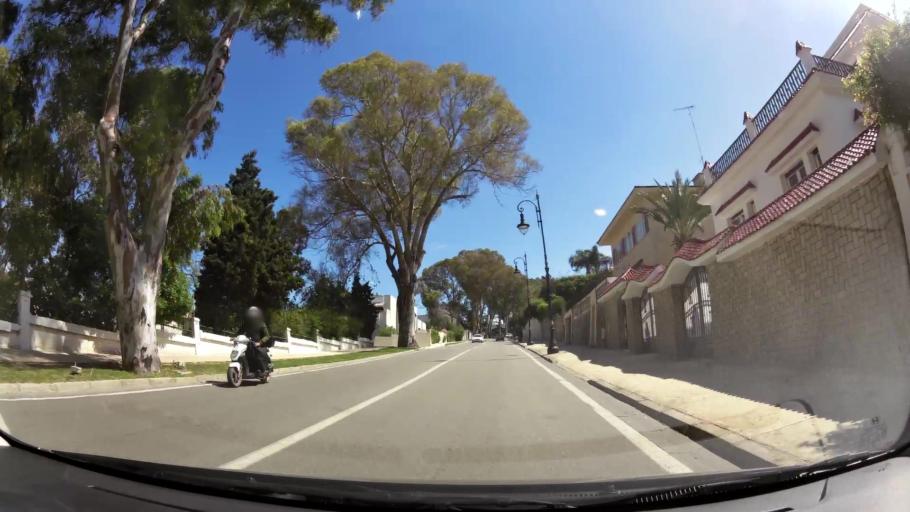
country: MA
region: Tanger-Tetouan
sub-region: Tanger-Assilah
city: Tangier
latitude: 35.7808
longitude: -5.8374
